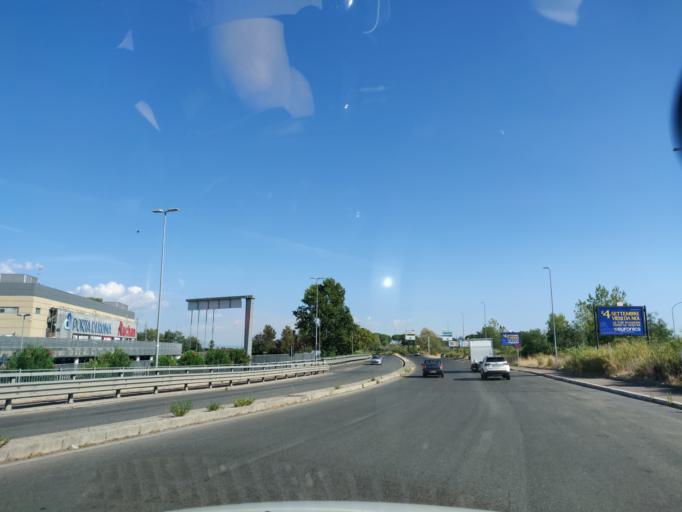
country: IT
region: Latium
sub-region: Citta metropolitana di Roma Capitale
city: Colle Verde
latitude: 41.9699
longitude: 12.5374
